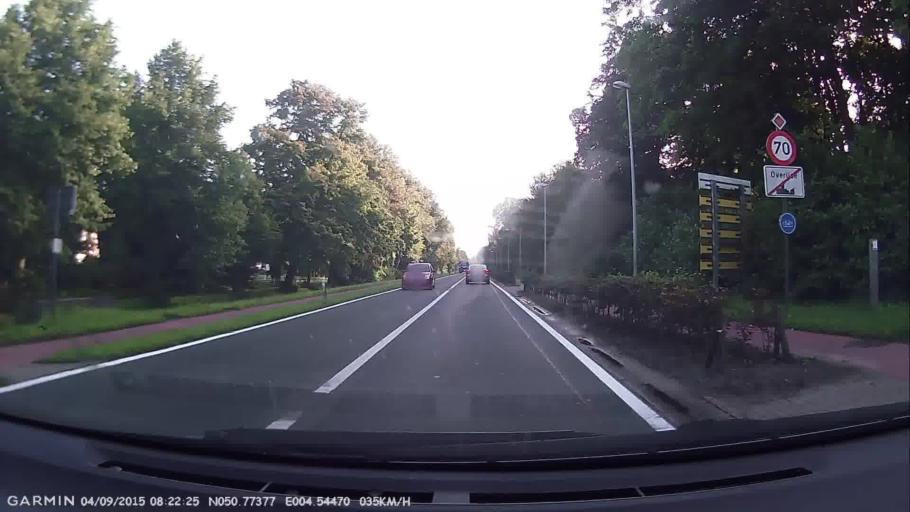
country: BE
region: Flanders
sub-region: Provincie Vlaams-Brabant
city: Overijse
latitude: 50.7738
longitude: 4.5448
